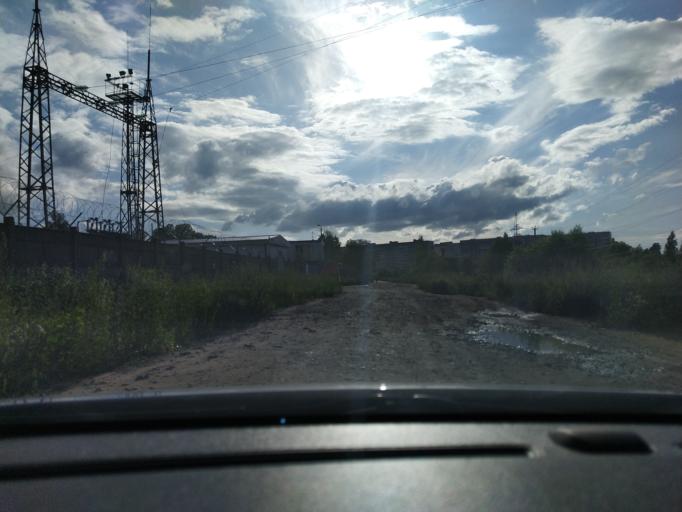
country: RU
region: St.-Petersburg
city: Gorelovo
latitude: 59.7848
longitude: 30.1581
